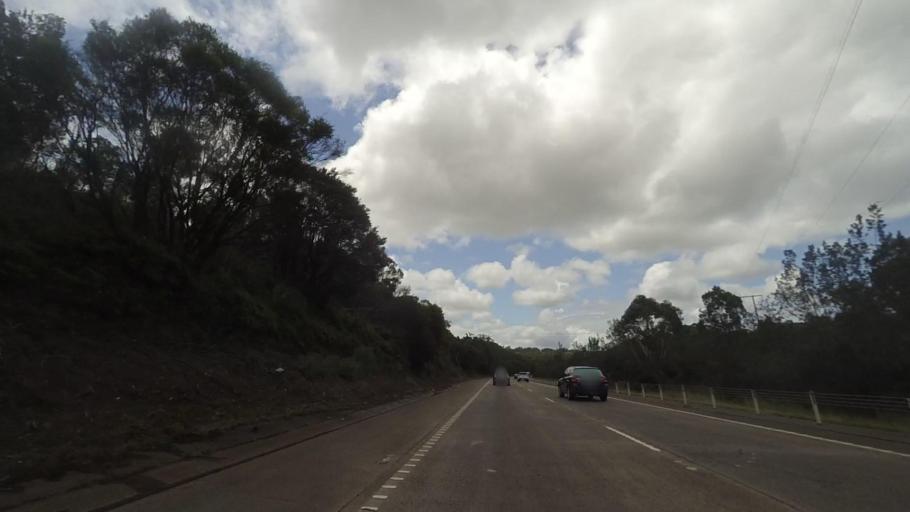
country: AU
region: New South Wales
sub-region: Gosford Shire
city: Narara
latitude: -33.3856
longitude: 151.2986
